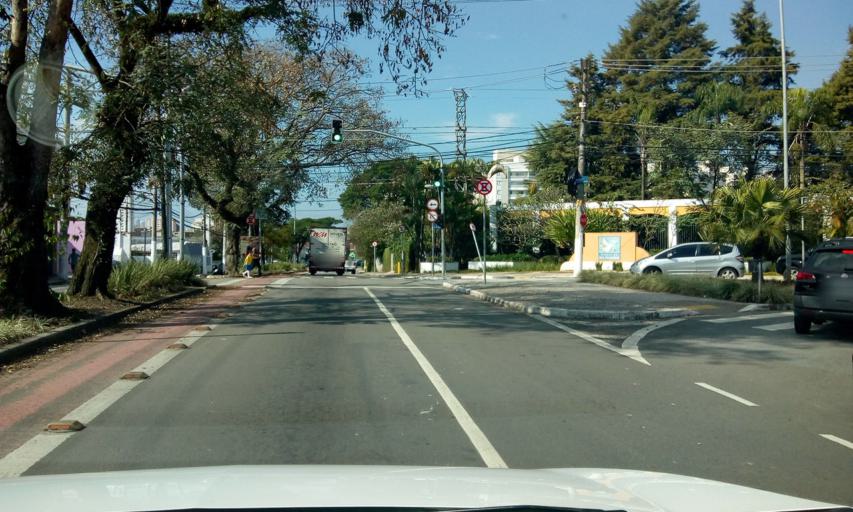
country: BR
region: Sao Paulo
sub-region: Osasco
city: Osasco
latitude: -23.5575
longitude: -46.7554
